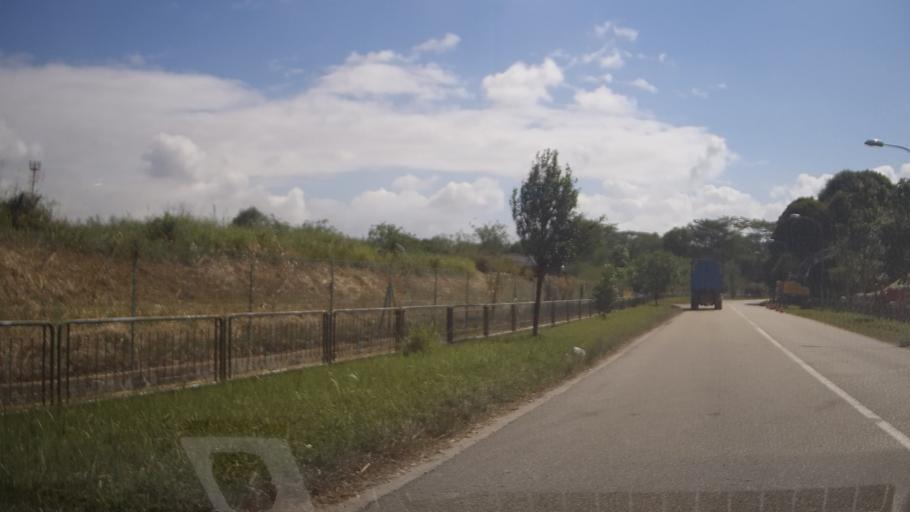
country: MY
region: Johor
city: Johor Bahru
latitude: 1.4333
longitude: 103.7114
